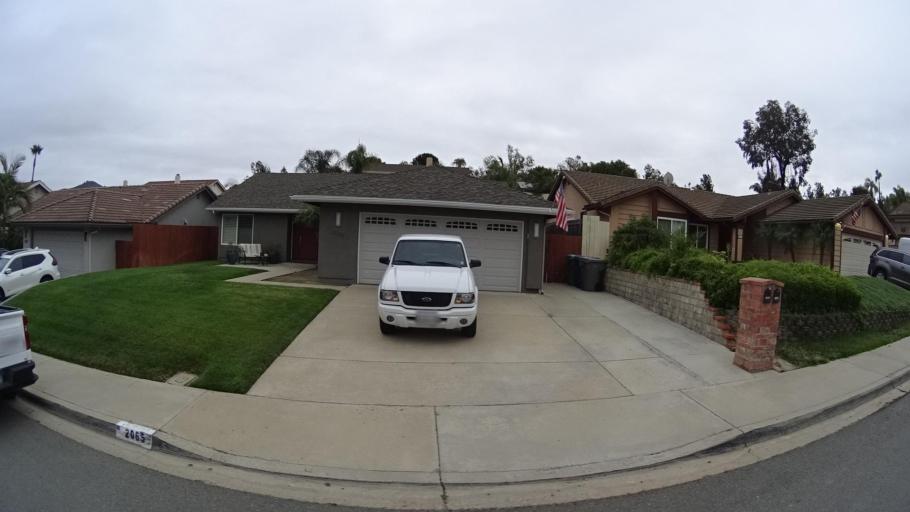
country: US
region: California
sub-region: San Diego County
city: Rancho San Diego
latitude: 32.7535
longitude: -116.9182
